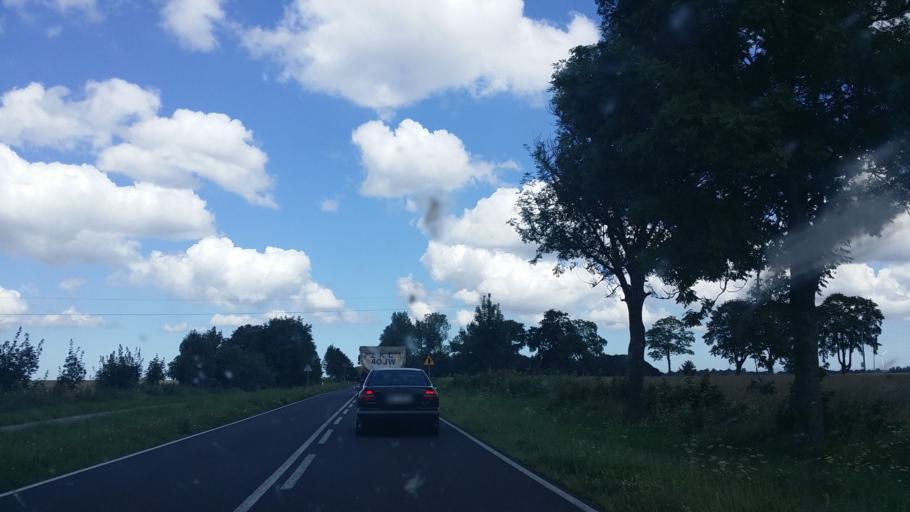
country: PL
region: West Pomeranian Voivodeship
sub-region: Powiat kolobrzeski
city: Goscino
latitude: 54.0164
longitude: 15.6605
